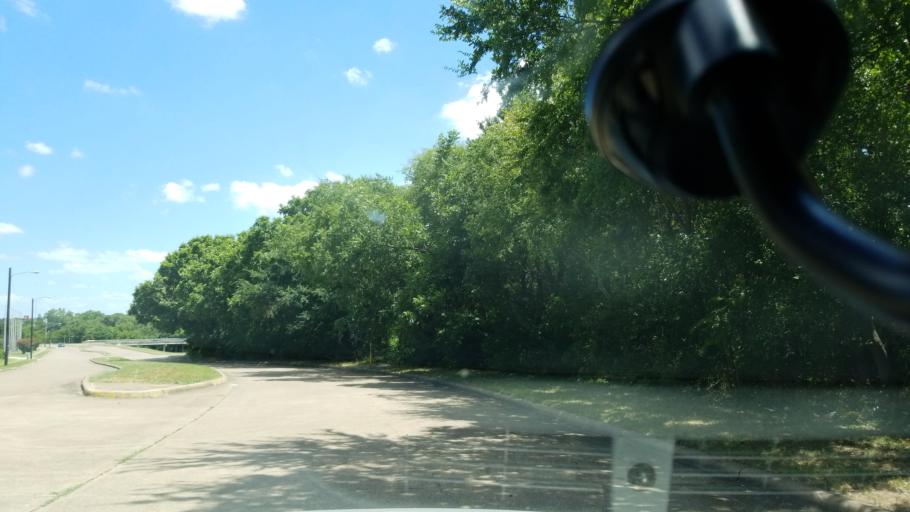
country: US
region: Texas
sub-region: Dallas County
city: Cockrell Hill
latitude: 32.6919
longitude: -96.8304
